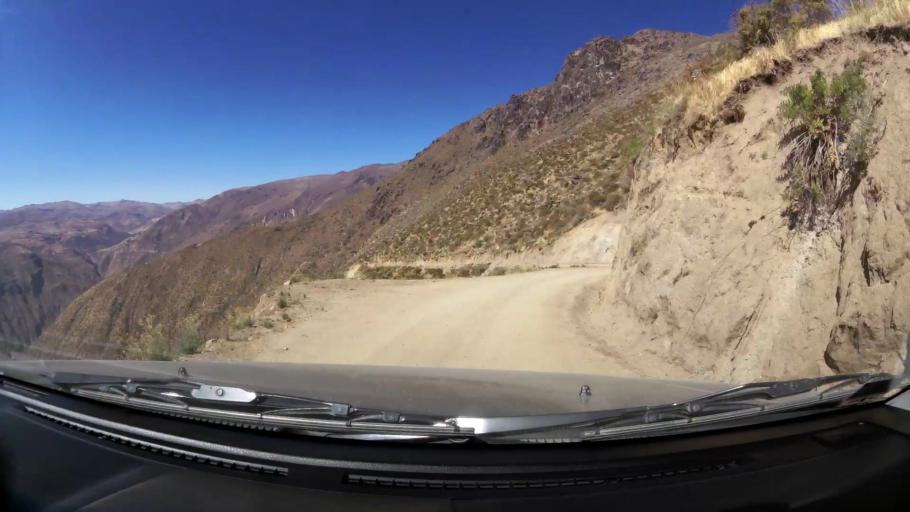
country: PE
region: Huancavelica
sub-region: Huaytara
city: Quito-Arma
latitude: -13.6231
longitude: -75.3516
